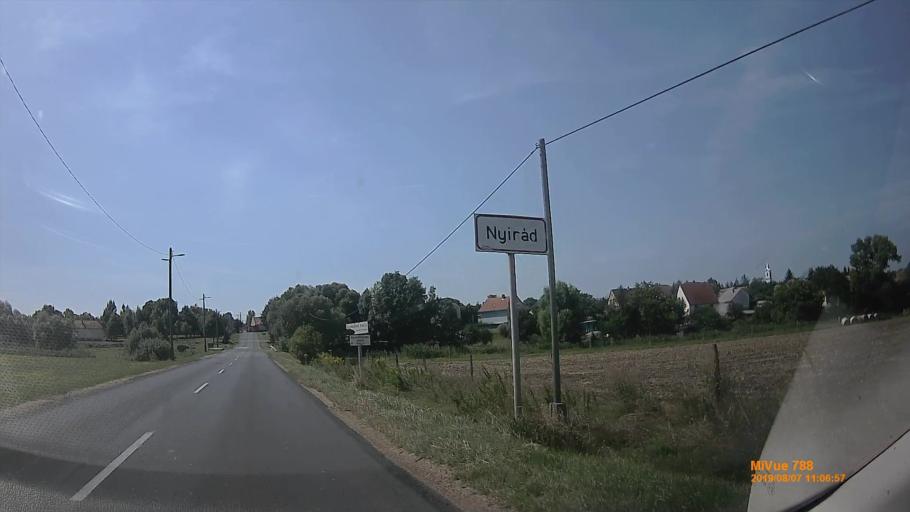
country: HU
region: Veszprem
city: Devecser
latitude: 47.0081
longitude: 17.4549
